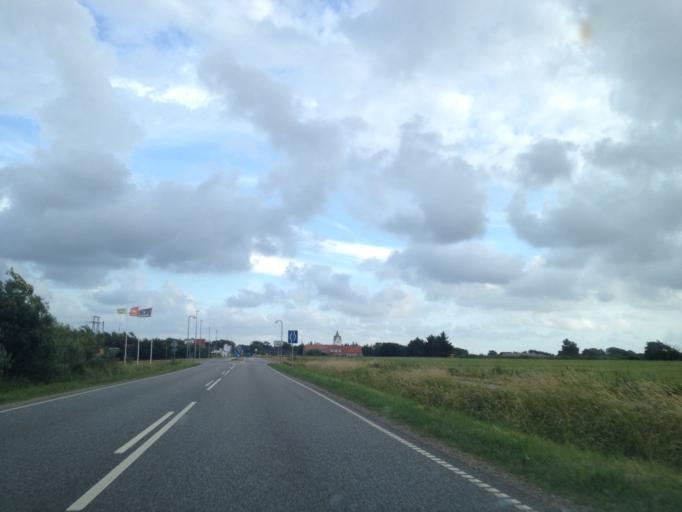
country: DK
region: South Denmark
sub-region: Tonder Kommune
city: Sherrebek
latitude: 55.1996
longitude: 8.7268
